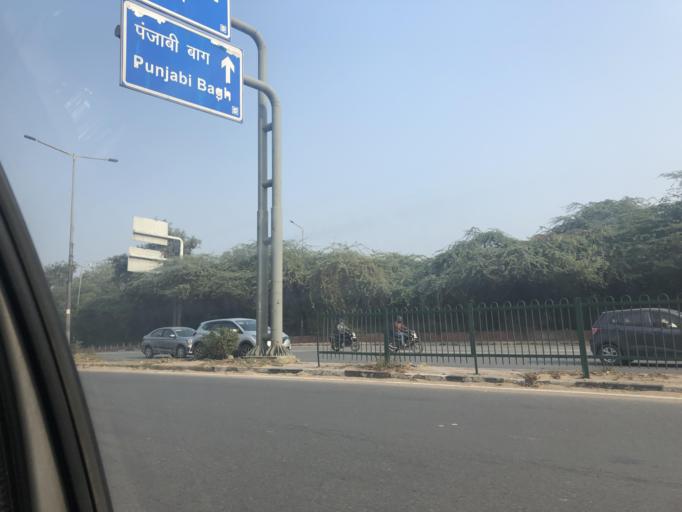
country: IN
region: NCT
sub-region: Central Delhi
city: Karol Bagh
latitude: 28.5981
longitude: 77.1637
